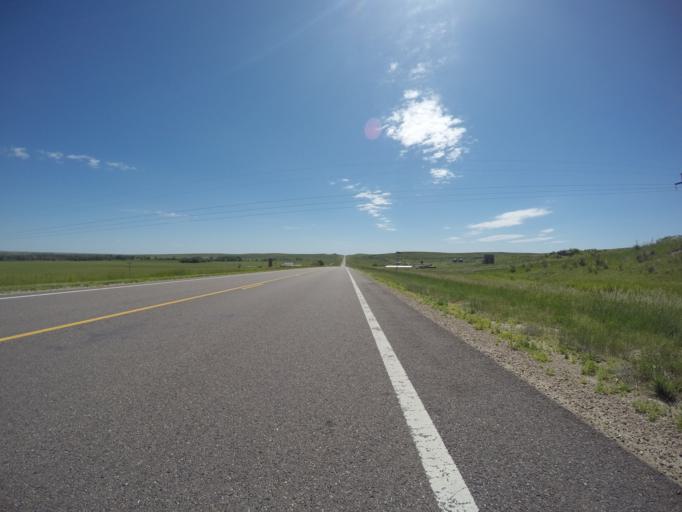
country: US
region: Kansas
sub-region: Rawlins County
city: Atwood
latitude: 39.8133
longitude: -101.0188
